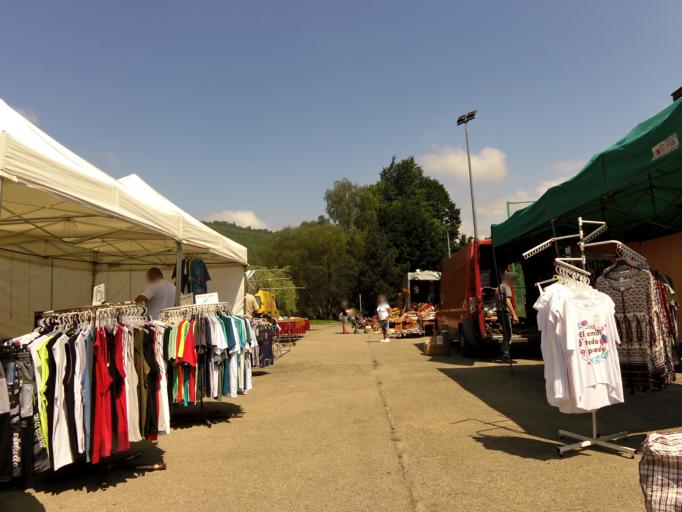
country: PL
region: Silesian Voivodeship
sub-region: Powiat zywiecki
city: Rajcza
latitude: 49.5037
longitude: 19.0992
